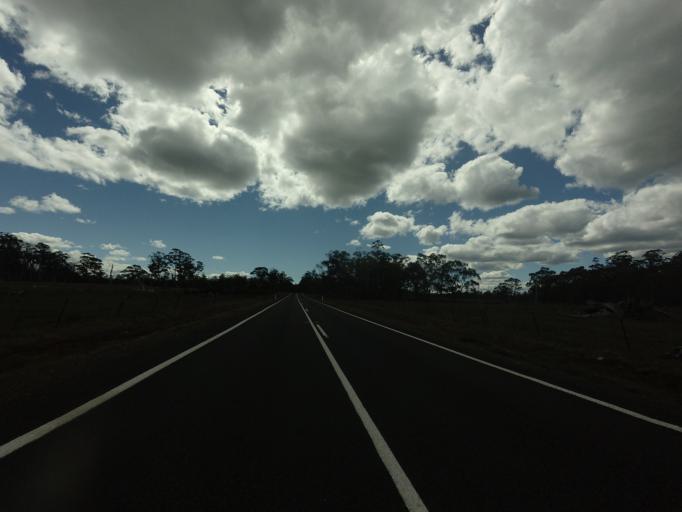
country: AU
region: Tasmania
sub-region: Northern Midlands
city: Evandale
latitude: -41.9792
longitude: 147.6608
